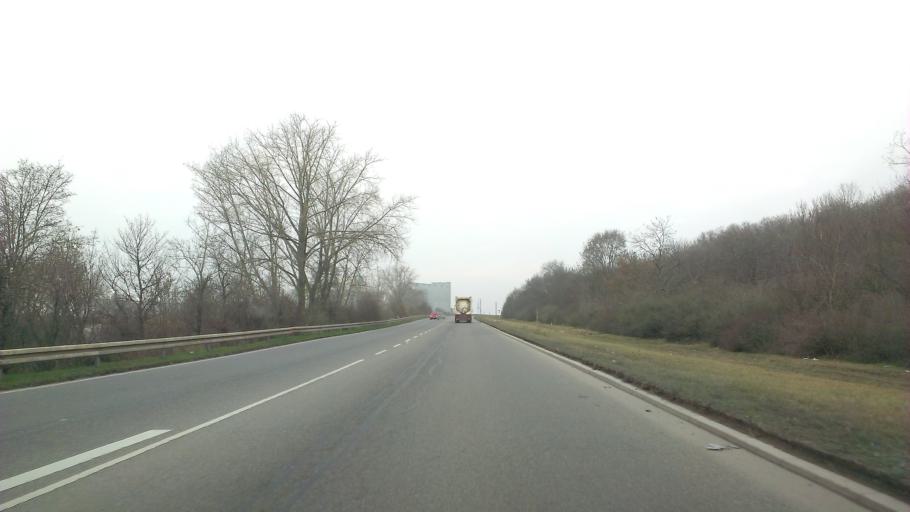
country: DE
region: Baden-Wuerttemberg
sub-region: Karlsruhe Region
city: Mannheim
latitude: 49.5287
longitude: 8.4537
